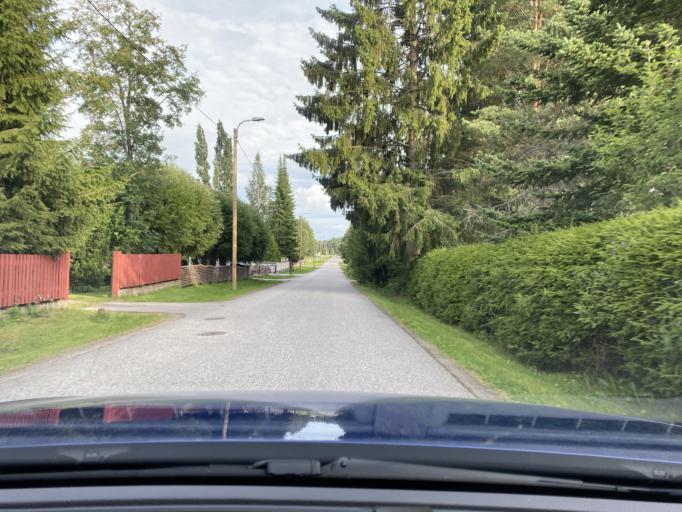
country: FI
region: Satakunta
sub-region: Rauma
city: Eura
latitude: 61.1162
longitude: 22.1425
